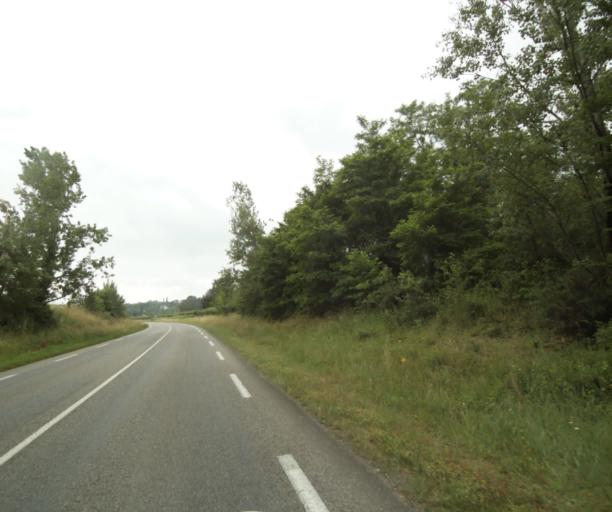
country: FR
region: Midi-Pyrenees
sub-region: Departement du Tarn-et-Garonne
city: Saint-Nauphary
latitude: 43.9837
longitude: 1.3931
